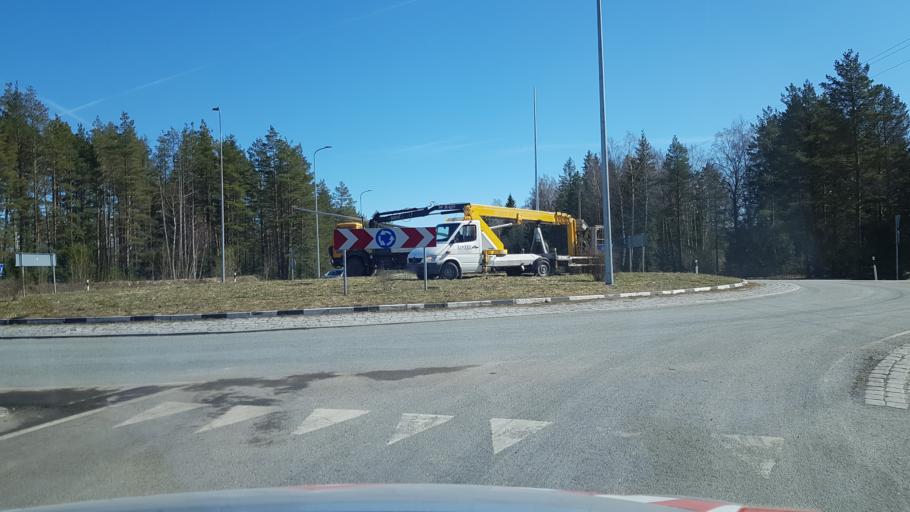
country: EE
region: Laeaene-Virumaa
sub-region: Someru vald
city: Someru
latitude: 59.3324
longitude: 26.4036
